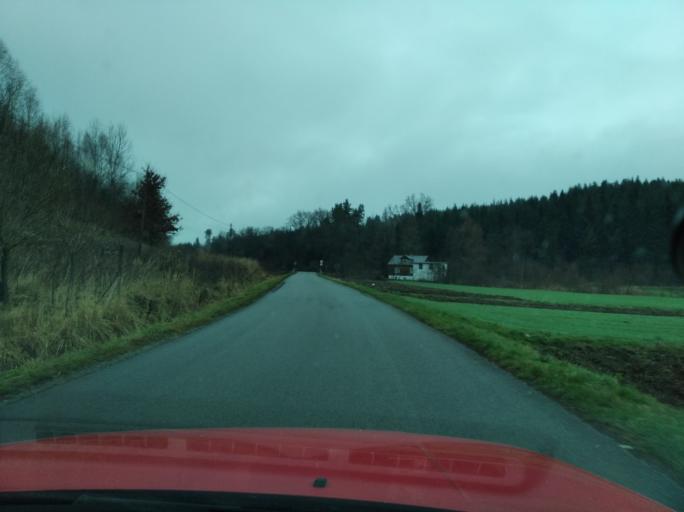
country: PL
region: Subcarpathian Voivodeship
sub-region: Powiat przemyski
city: Nienadowa
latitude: 49.8574
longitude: 22.4261
